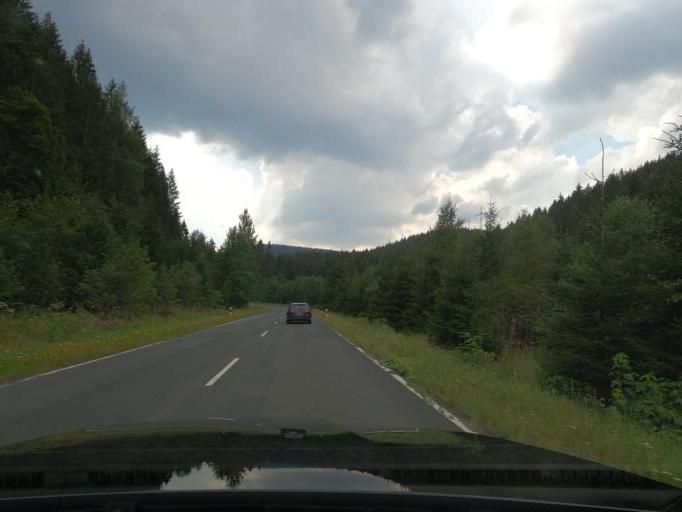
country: DE
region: Lower Saxony
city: Wildemann
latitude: 51.8472
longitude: 10.2678
